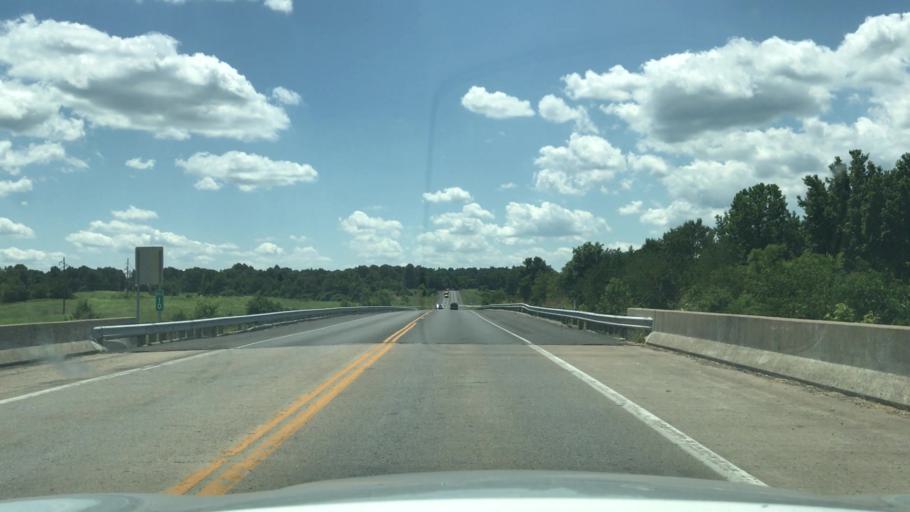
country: US
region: Kentucky
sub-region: Muhlenberg County
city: Greenville
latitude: 37.2131
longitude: -87.1914
